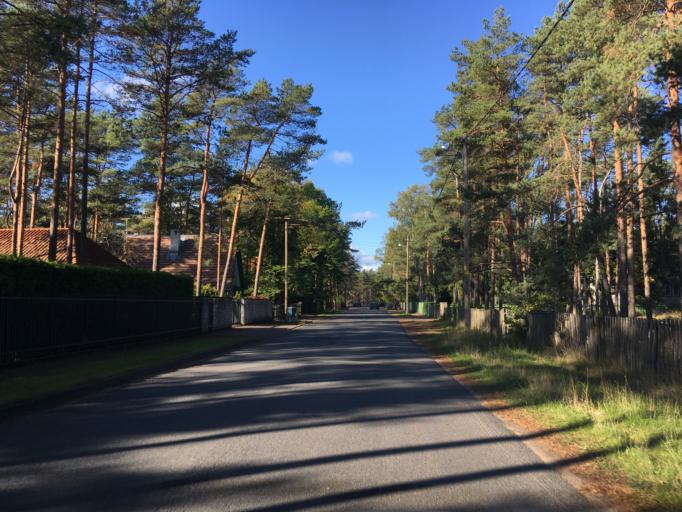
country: EE
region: Harju
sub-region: Saue vald
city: Laagri
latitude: 59.3751
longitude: 24.6832
